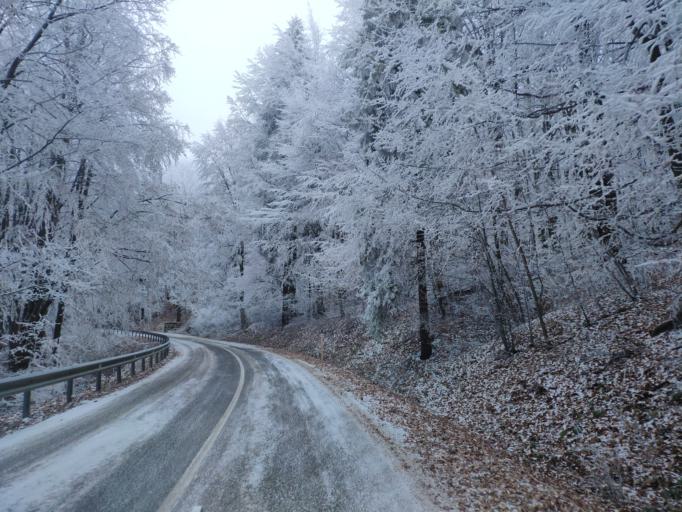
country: SK
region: Kosicky
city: Dobsina
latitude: 48.8051
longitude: 20.4861
